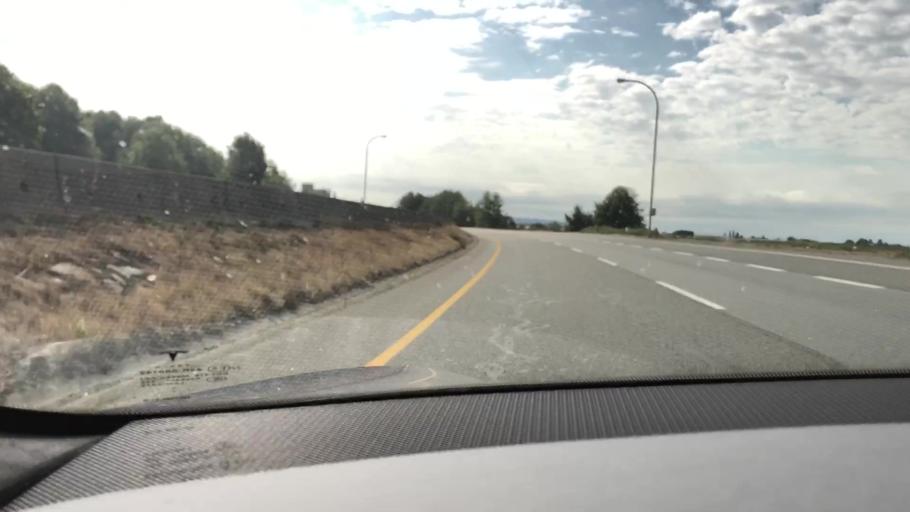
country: CA
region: British Columbia
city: Delta
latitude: 49.1189
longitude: -122.9264
